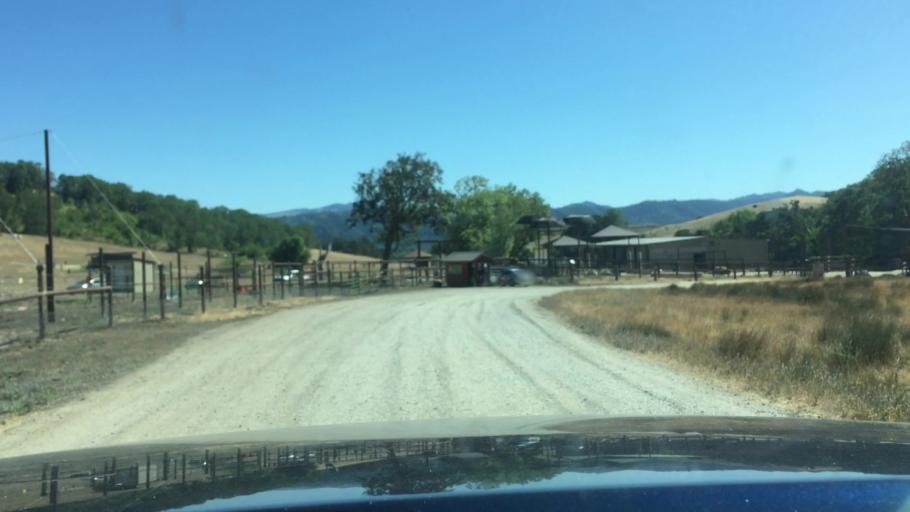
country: US
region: Oregon
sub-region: Douglas County
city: Winston
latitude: 43.1376
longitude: -123.4324
